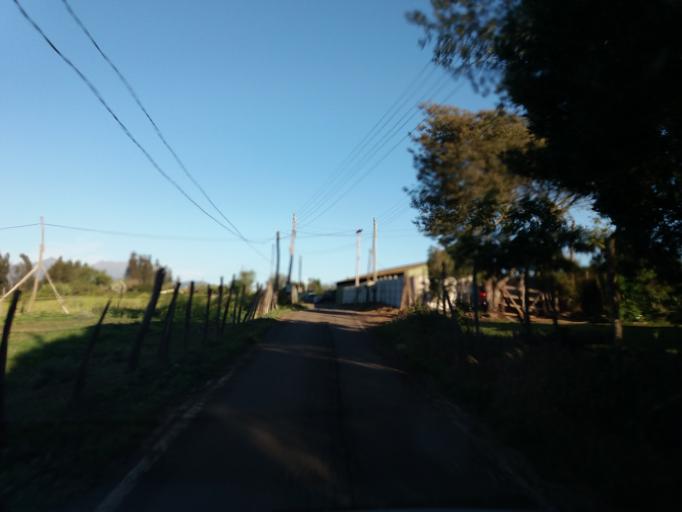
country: CL
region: Valparaiso
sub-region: Provincia de Quillota
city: Quillota
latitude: -32.9126
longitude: -71.3418
